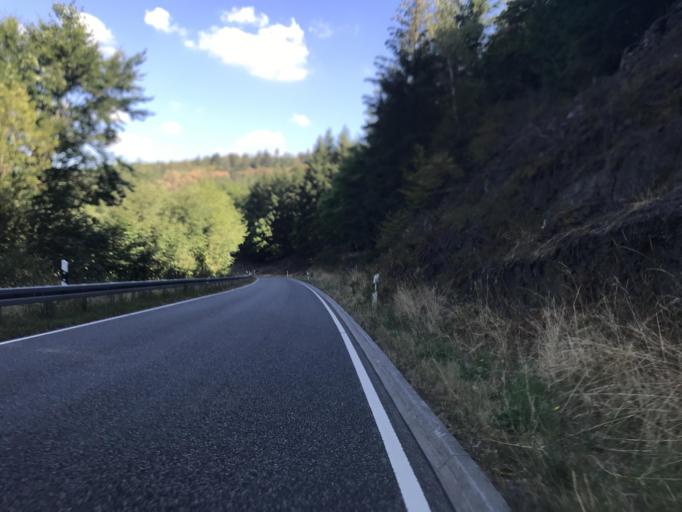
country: DE
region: Hesse
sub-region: Regierungsbezirk Darmstadt
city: Bad Schwalbach
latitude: 50.0851
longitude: 8.0199
